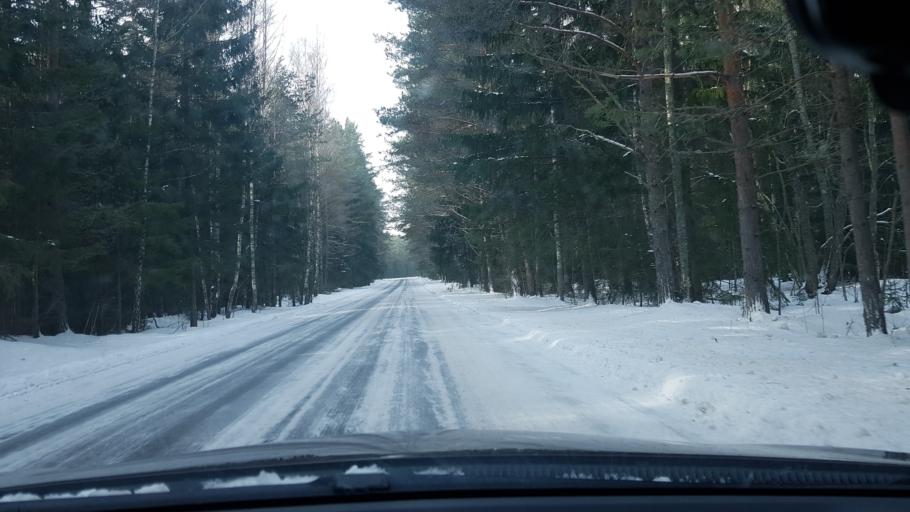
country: EE
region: Harju
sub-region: Kuusalu vald
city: Kuusalu
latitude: 59.5568
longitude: 25.5556
